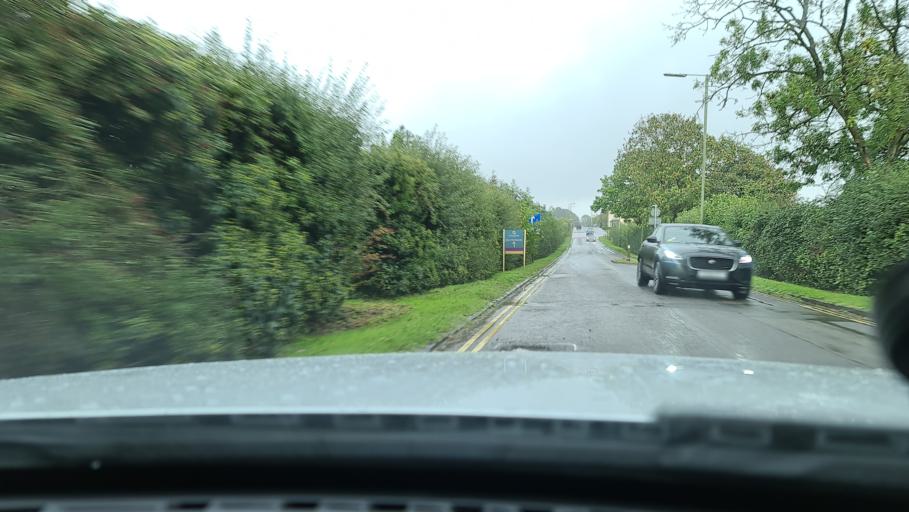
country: GB
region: England
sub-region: Oxfordshire
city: Somerton
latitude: 51.9293
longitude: -1.2674
